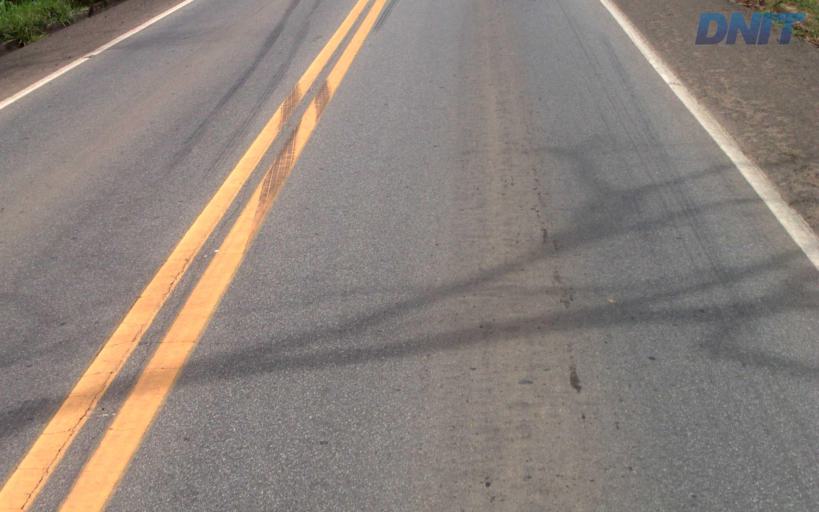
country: BR
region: Minas Gerais
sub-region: Ipaba
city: Ipaba
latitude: -19.3309
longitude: -42.4213
